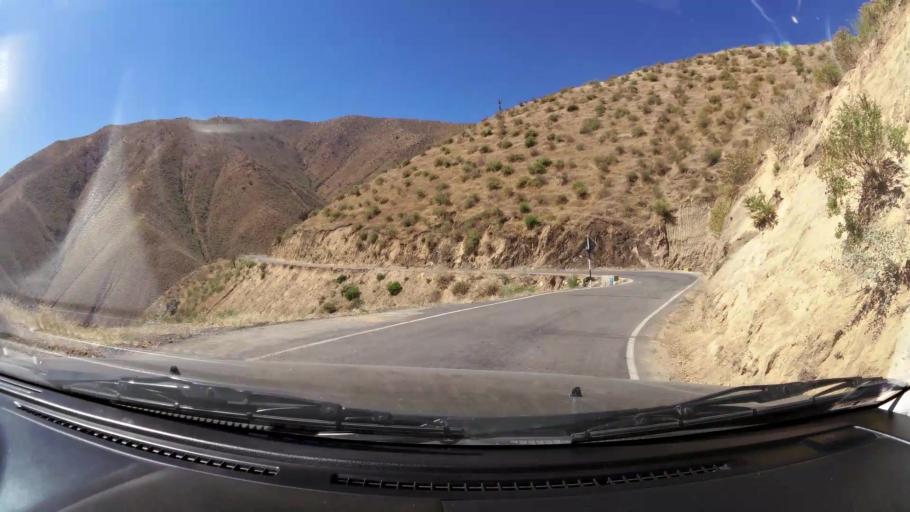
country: PE
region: Ica
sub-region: Provincia de Pisco
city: Huancano
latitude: -13.7227
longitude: -75.4572
